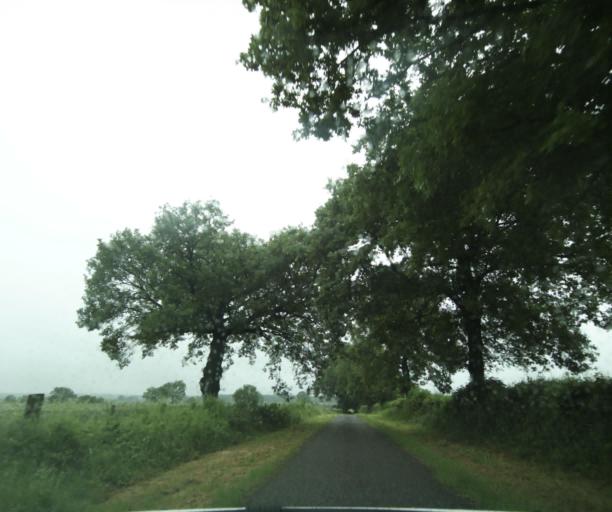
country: FR
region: Bourgogne
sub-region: Departement de Saone-et-Loire
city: Paray-le-Monial
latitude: 46.4650
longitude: 4.1999
